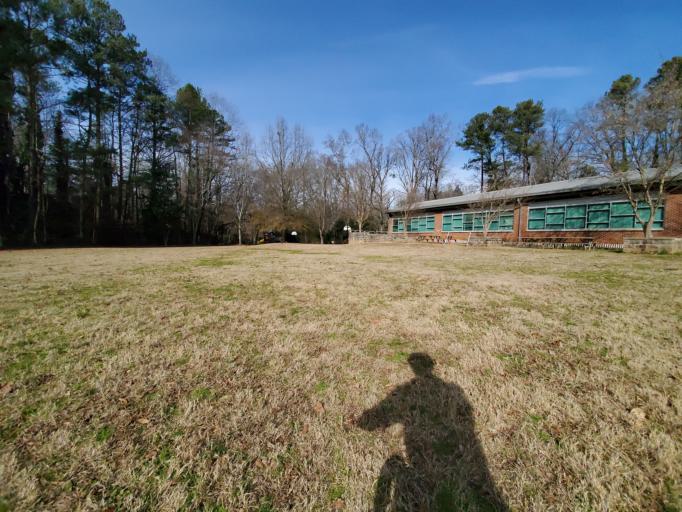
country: US
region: Georgia
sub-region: DeKalb County
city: North Decatur
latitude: 33.7831
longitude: -84.3067
